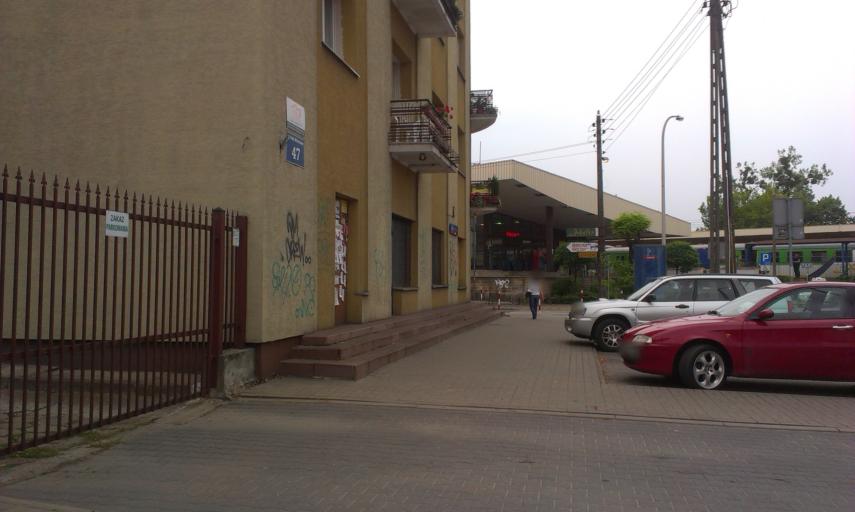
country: PL
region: Masovian Voivodeship
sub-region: Warszawa
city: Ursus
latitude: 52.1956
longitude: 20.8851
